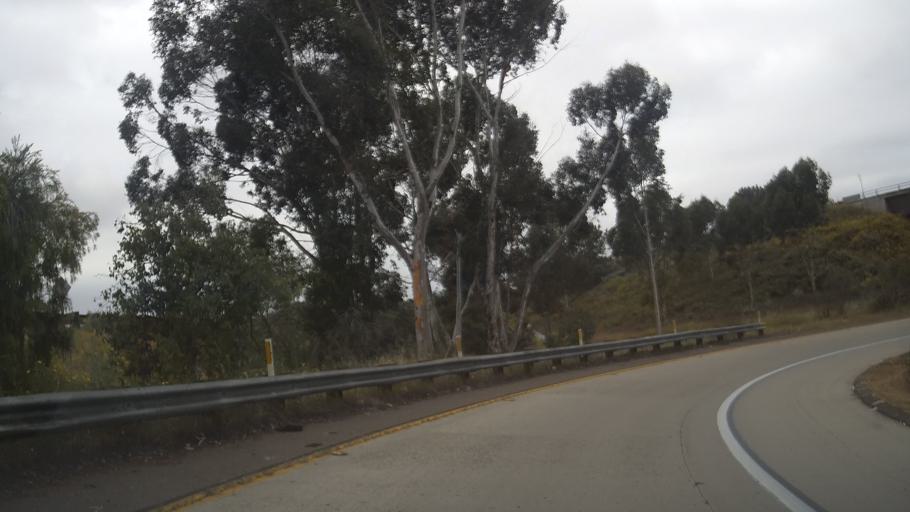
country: US
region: California
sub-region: San Diego County
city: Chula Vista
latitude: 32.6573
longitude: -117.0755
